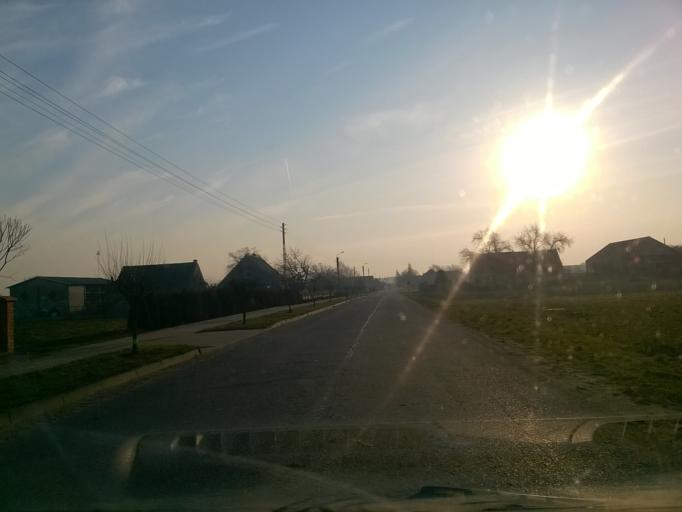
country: PL
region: Kujawsko-Pomorskie
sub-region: Powiat tucholski
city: Gostycyn
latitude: 53.4803
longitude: 17.7411
